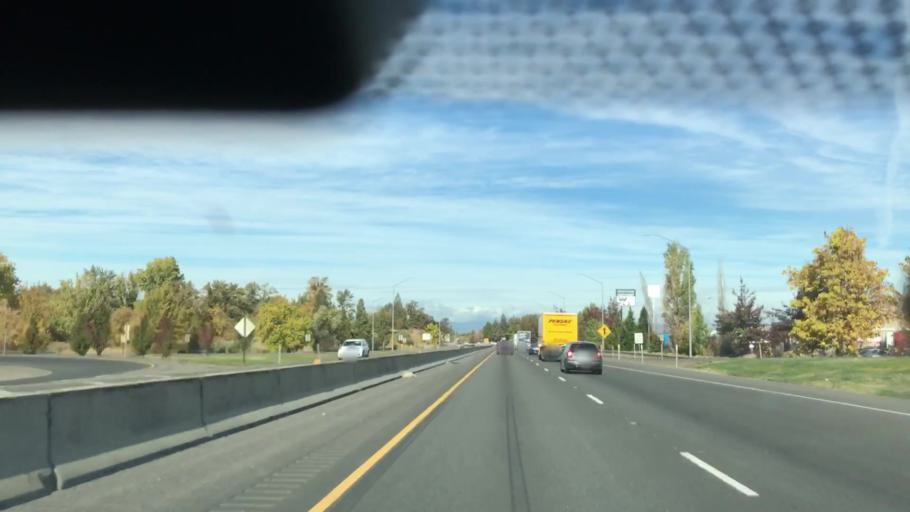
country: US
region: Oregon
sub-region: Jackson County
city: Medford
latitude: 42.3513
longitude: -122.8769
